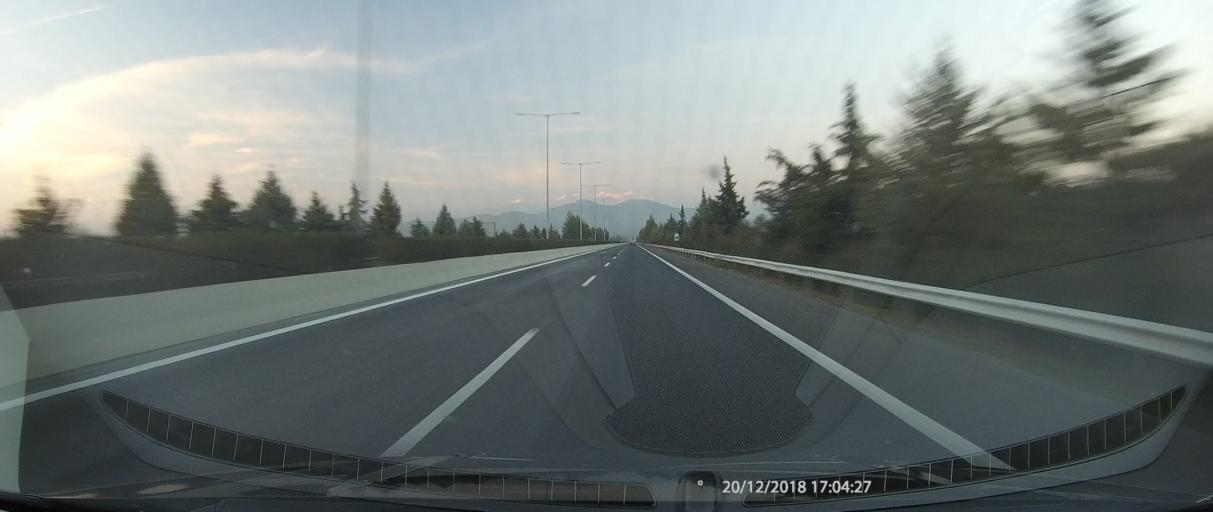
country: GR
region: Thessaly
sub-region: Nomos Larisis
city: Makrychori
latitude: 39.7181
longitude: 22.4822
